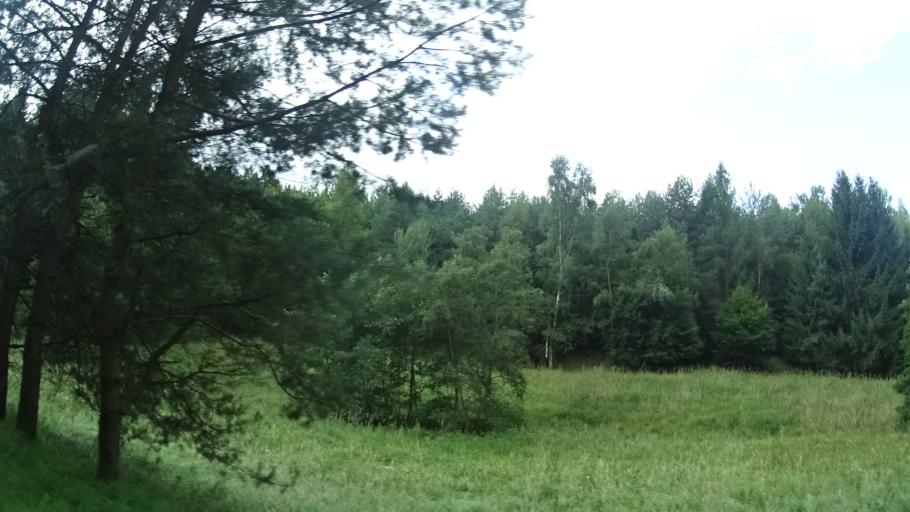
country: DE
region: Thuringia
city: Unterwellenborn
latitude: 50.6801
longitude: 11.4161
